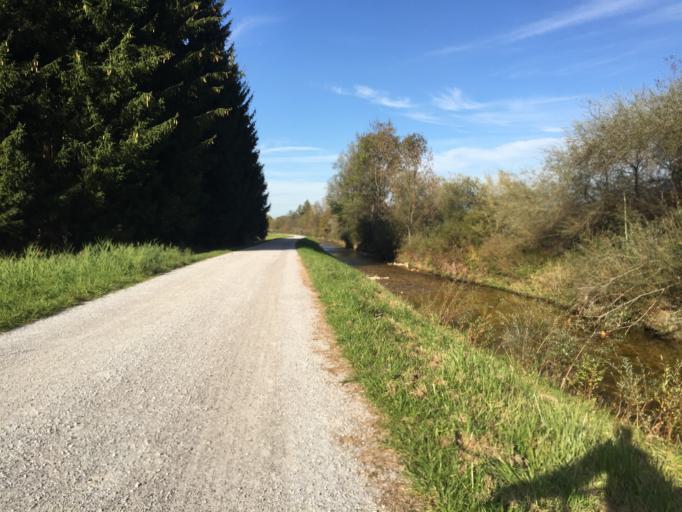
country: AT
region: Salzburg
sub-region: Politischer Bezirk Salzburg-Umgebung
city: Grodig
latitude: 47.7577
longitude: 12.9971
